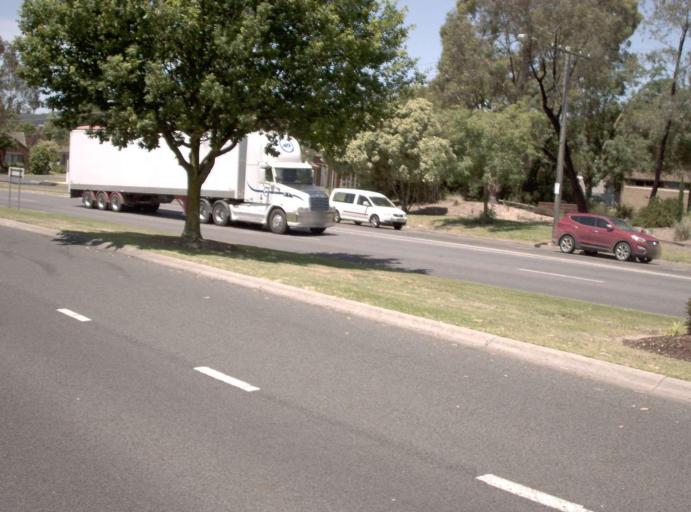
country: AU
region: Victoria
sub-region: Latrobe
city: Moe
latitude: -38.2075
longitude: 146.1566
